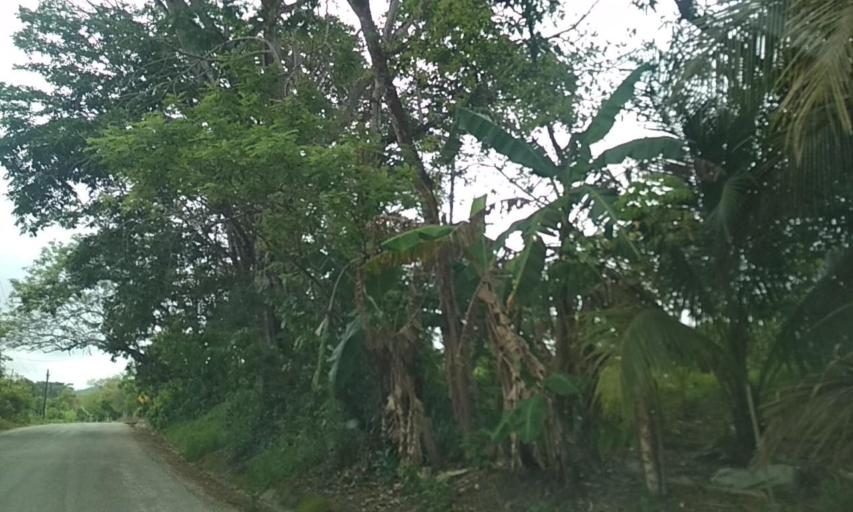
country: MX
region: Veracruz
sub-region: Uxpanapa
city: Poblado 10
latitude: 17.5095
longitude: -94.1585
